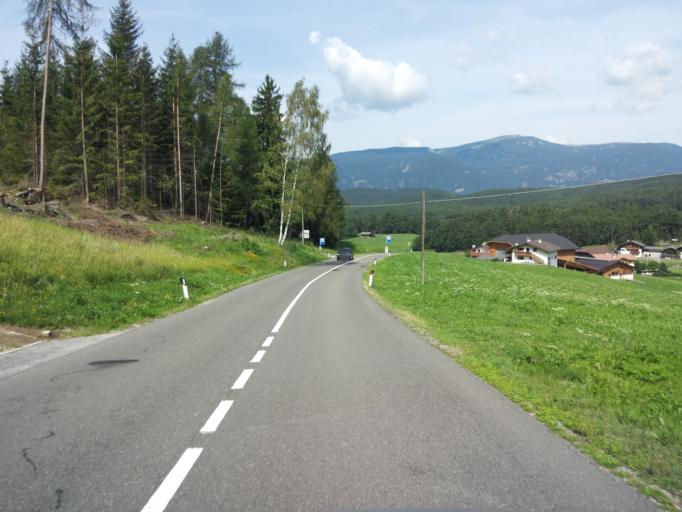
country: IT
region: Trentino-Alto Adige
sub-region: Bolzano
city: Castelrotto
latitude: 46.5711
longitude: 11.5823
